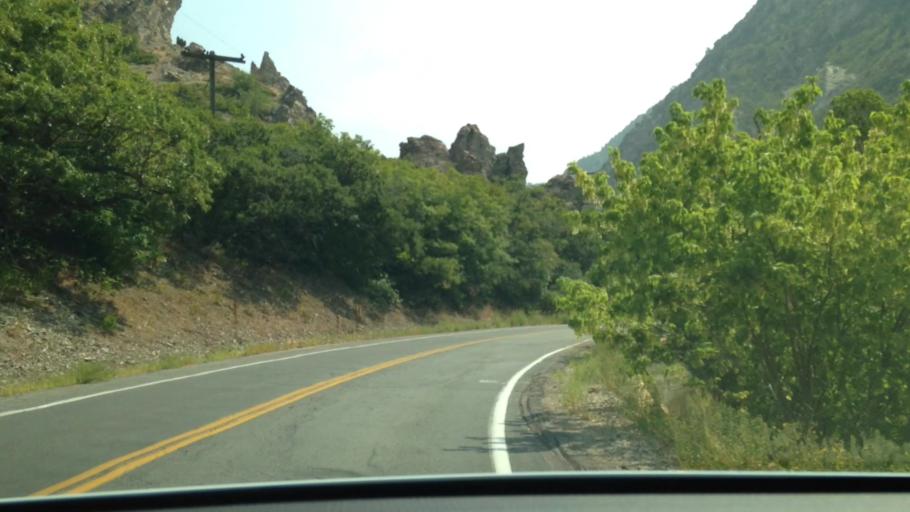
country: US
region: Utah
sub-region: Salt Lake County
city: Mount Olympus
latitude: 40.6907
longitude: -111.7776
